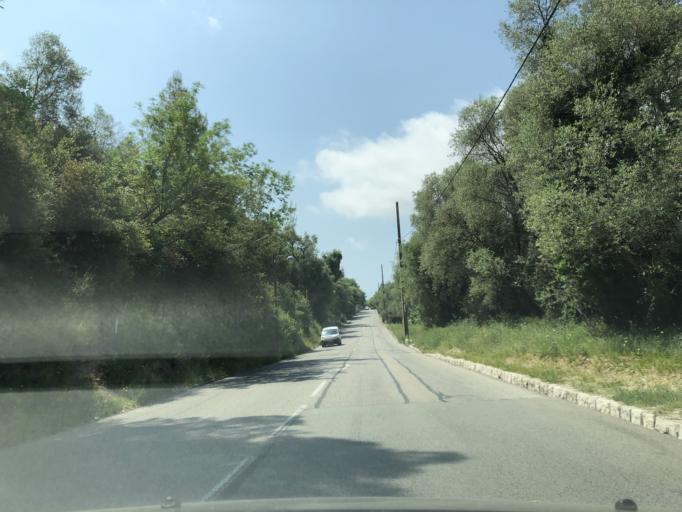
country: FR
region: Provence-Alpes-Cote d'Azur
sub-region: Departement des Alpes-Maritimes
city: Saint-Andre-de-la-Roche
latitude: 43.7289
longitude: 7.2956
